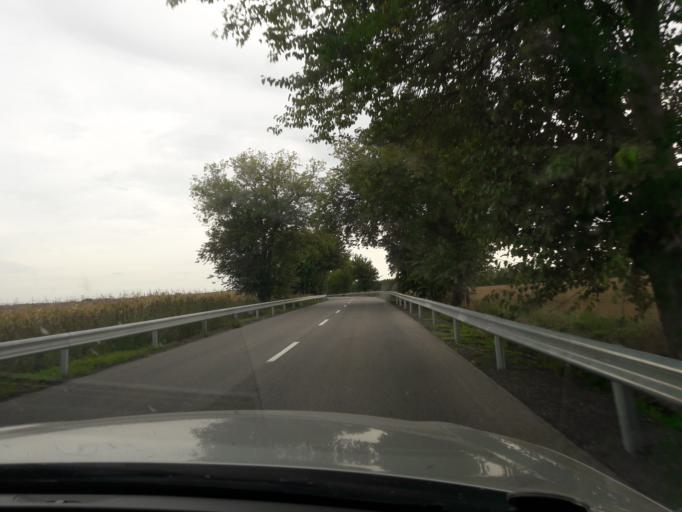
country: SK
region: Nitriansky
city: Tlmace
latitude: 48.1692
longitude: 18.4515
